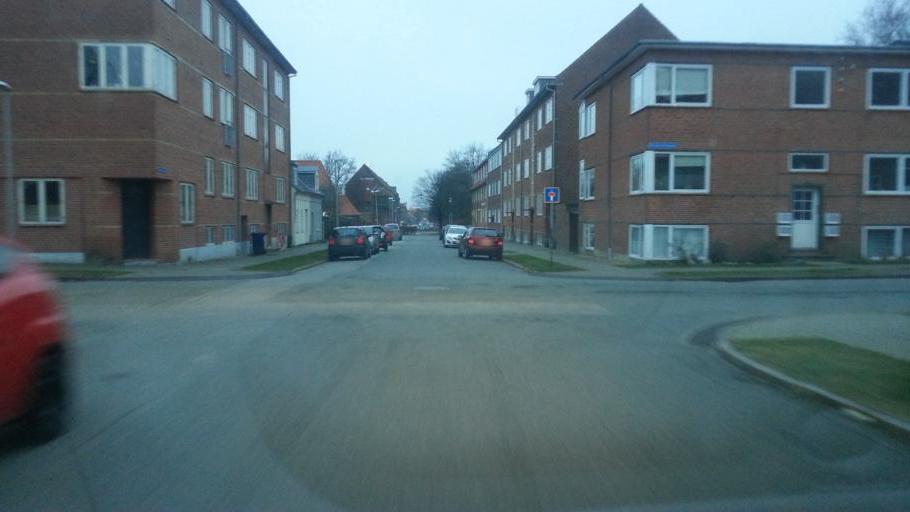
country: DK
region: South Denmark
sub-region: Esbjerg Kommune
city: Esbjerg
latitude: 55.4743
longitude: 8.4480
